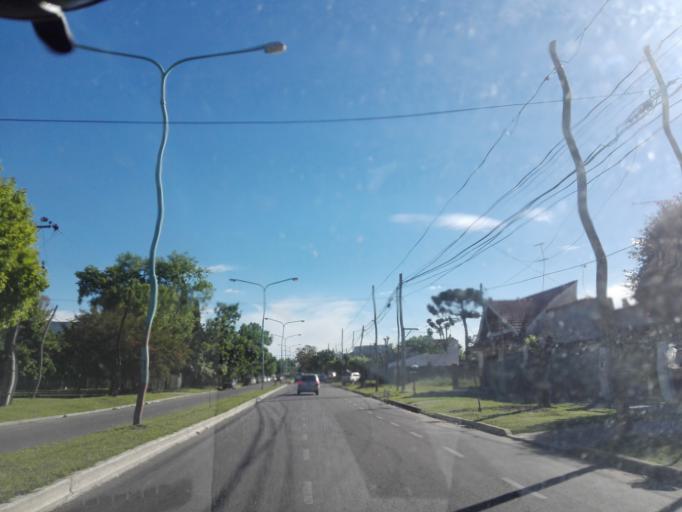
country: AR
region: Buenos Aires
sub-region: Partido de La Plata
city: La Plata
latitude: -34.8900
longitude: -58.0066
